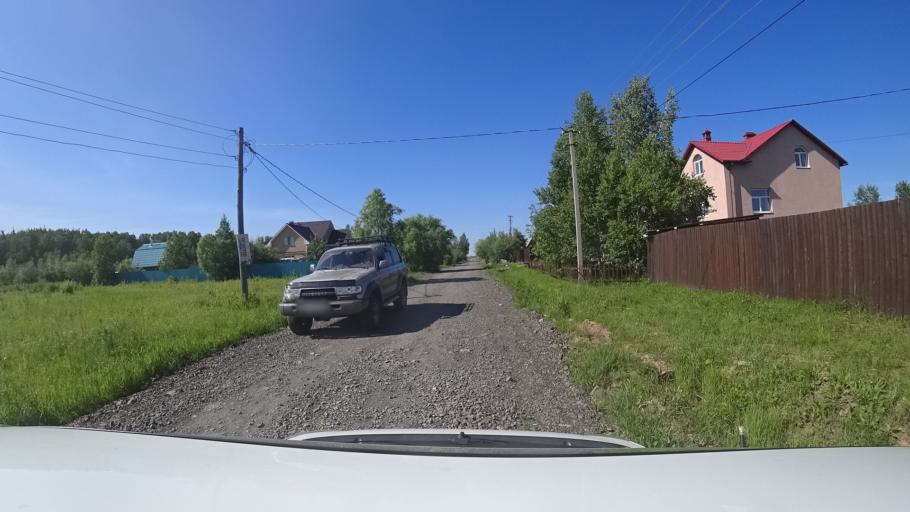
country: RU
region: Khabarovsk Krai
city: Topolevo
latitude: 48.5511
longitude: 135.1691
